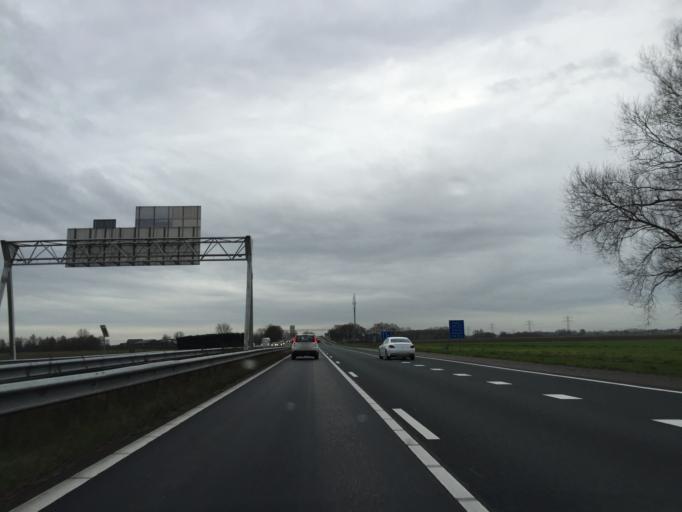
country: NL
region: North Brabant
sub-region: Roosendaal
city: Roosendaal
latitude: 51.5226
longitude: 4.4241
